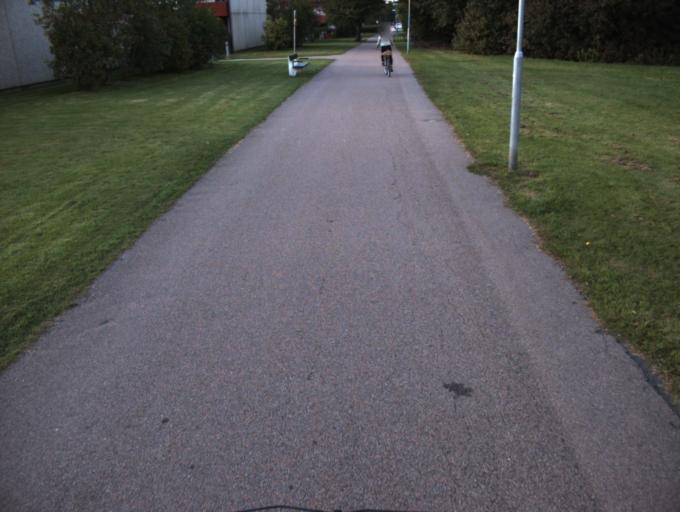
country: SE
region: Skane
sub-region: Helsingborg
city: Odakra
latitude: 56.0701
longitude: 12.7355
